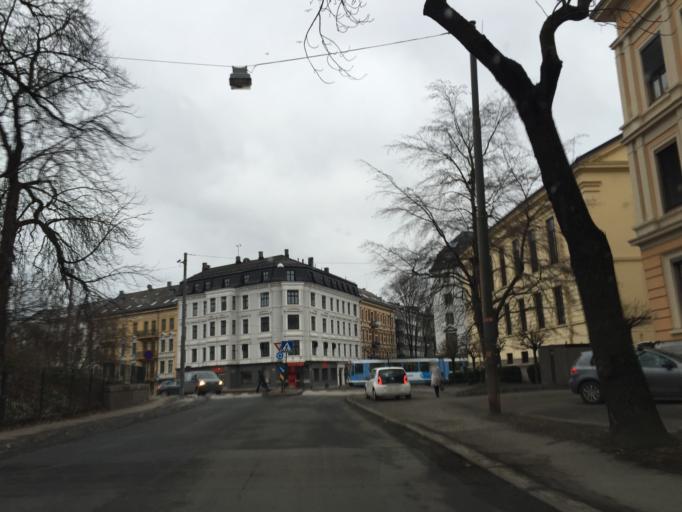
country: NO
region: Oslo
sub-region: Oslo
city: Oslo
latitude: 59.9159
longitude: 10.7227
